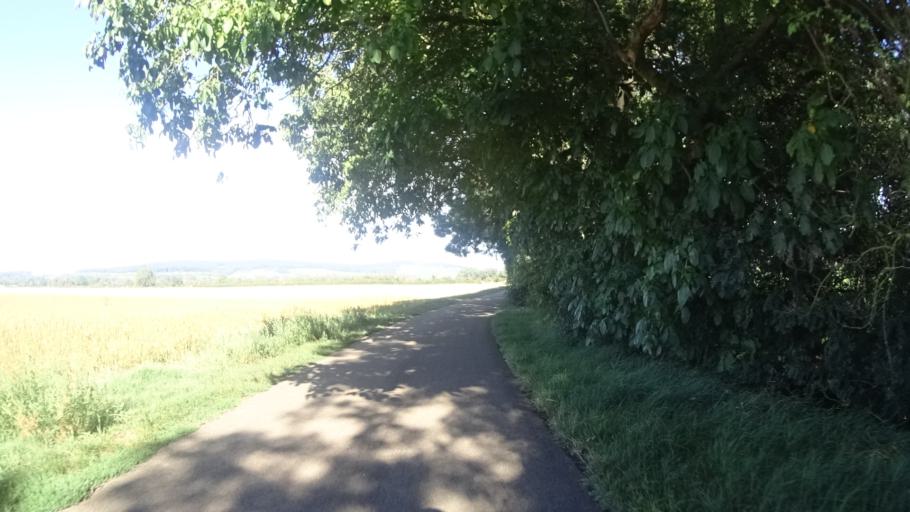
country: FR
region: Bourgogne
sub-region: Departement de la Nievre
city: Pouilly-sur-Loire
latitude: 47.3072
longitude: 2.8969
